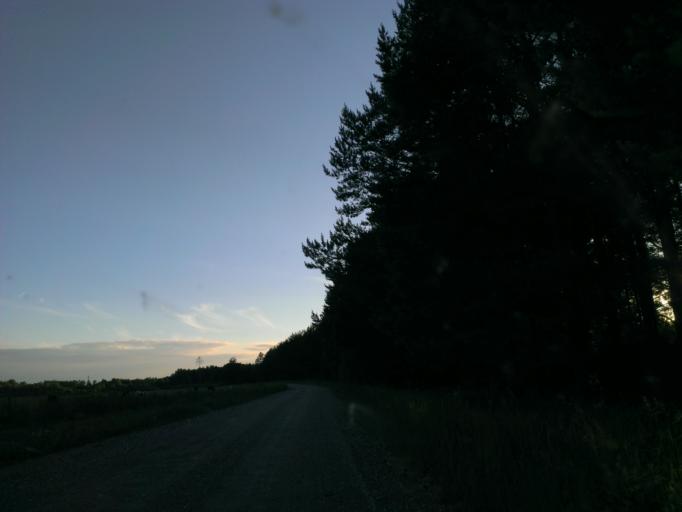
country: LT
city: Skuodas
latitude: 56.3260
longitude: 21.3462
